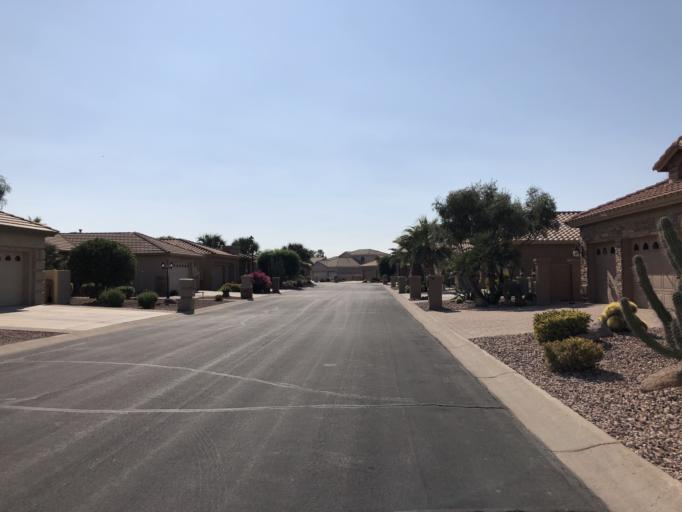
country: US
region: Arizona
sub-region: Maricopa County
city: Sun Lakes
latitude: 33.2275
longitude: -111.8872
